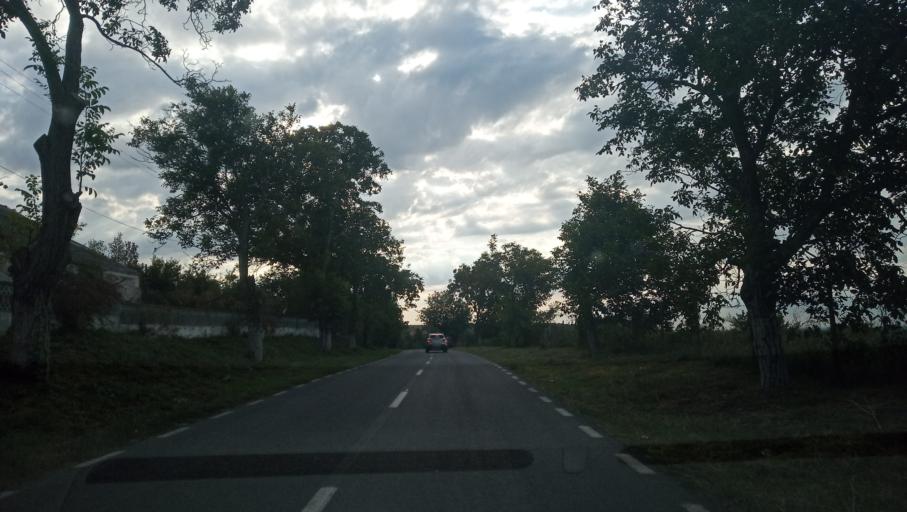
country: RO
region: Constanta
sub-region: Comuna Ostrov
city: Ostrov
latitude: 44.1026
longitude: 27.3749
